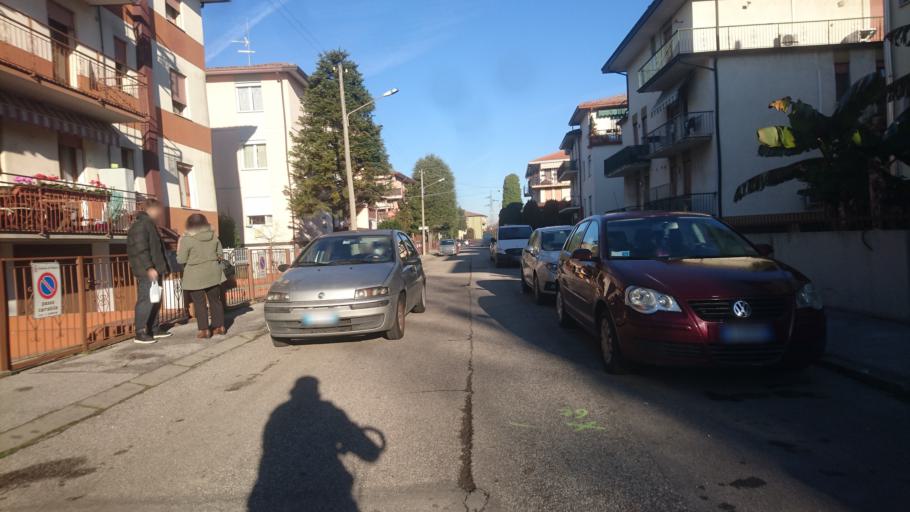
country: IT
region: Veneto
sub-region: Provincia di Padova
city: Padova
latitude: 45.4292
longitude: 11.8711
